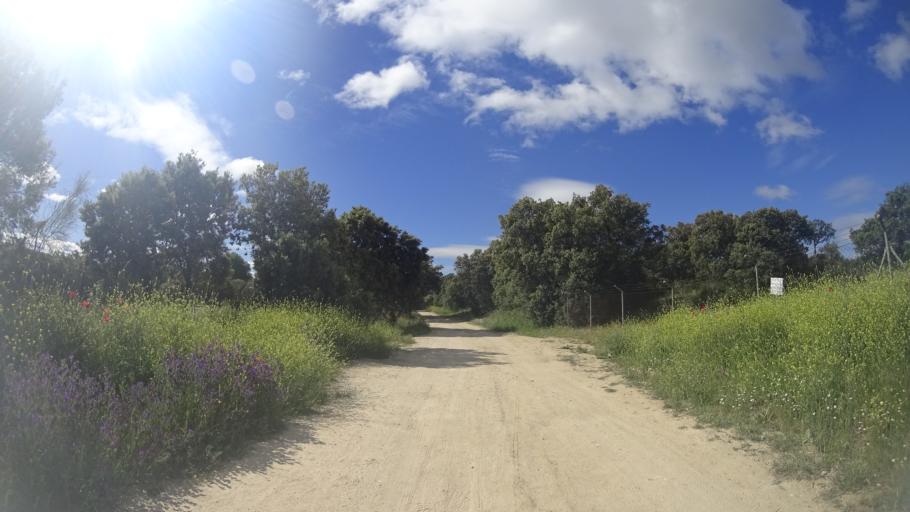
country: ES
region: Madrid
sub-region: Provincia de Madrid
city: Villanueva del Pardillo
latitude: 40.4425
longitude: -3.9536
